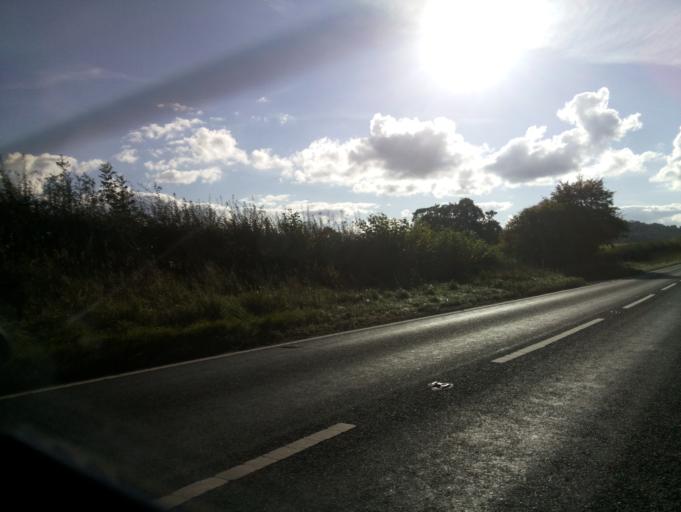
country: GB
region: Wales
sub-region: Sir Powys
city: Brecon
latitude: 52.0032
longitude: -3.2629
